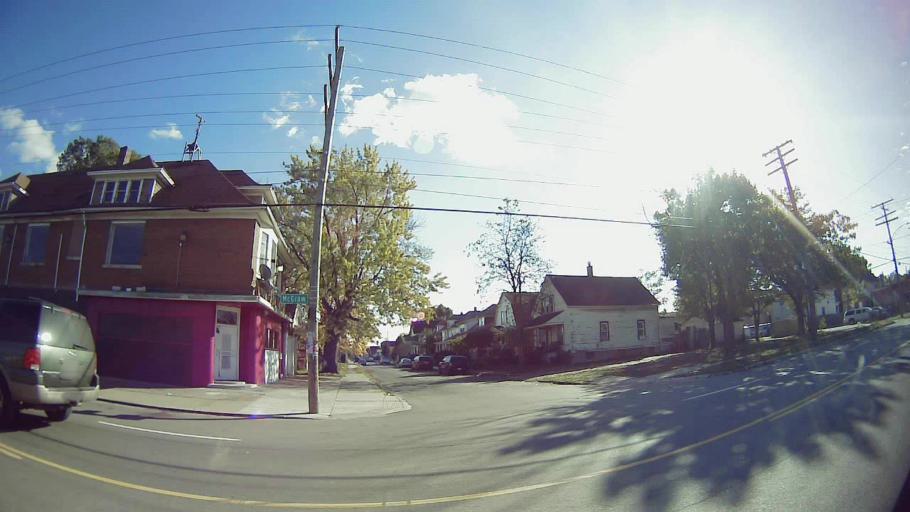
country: US
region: Michigan
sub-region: Wayne County
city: Dearborn
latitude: 42.3365
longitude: -83.1382
